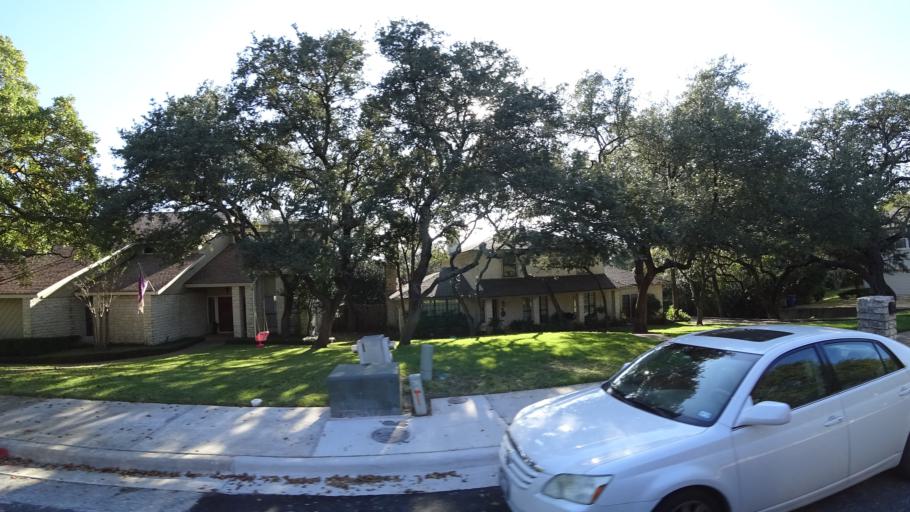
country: US
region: Texas
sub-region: Williamson County
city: Anderson Mill
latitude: 30.4426
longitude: -97.8113
